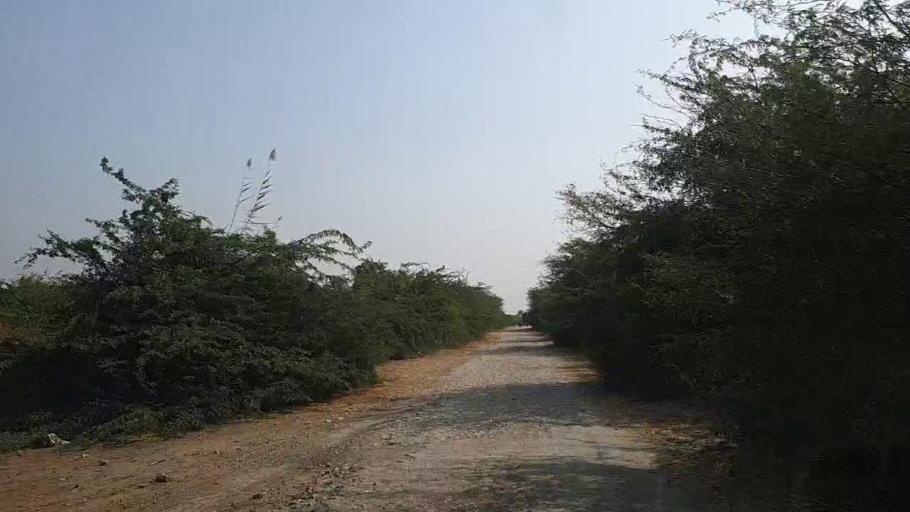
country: PK
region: Sindh
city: Keti Bandar
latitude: 24.2477
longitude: 67.6331
